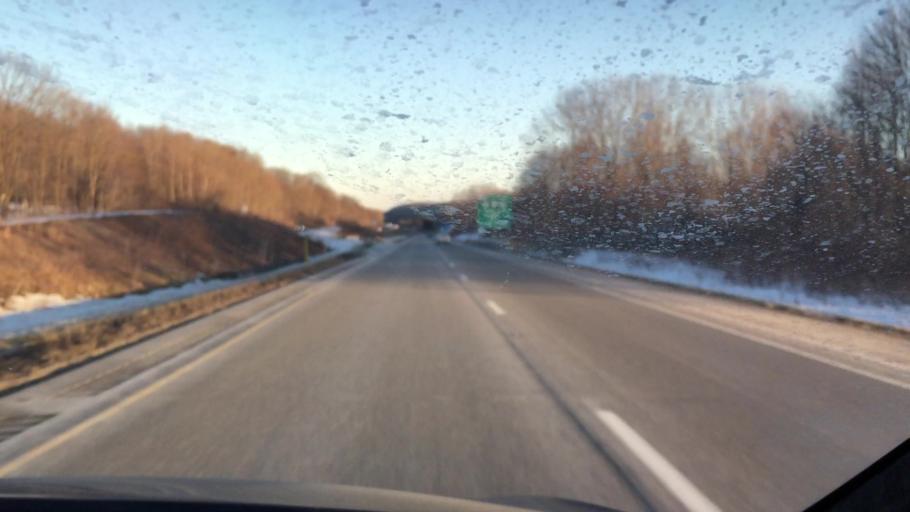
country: US
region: Pennsylvania
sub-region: Crawford County
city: Meadville
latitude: 41.6375
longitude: -80.1974
